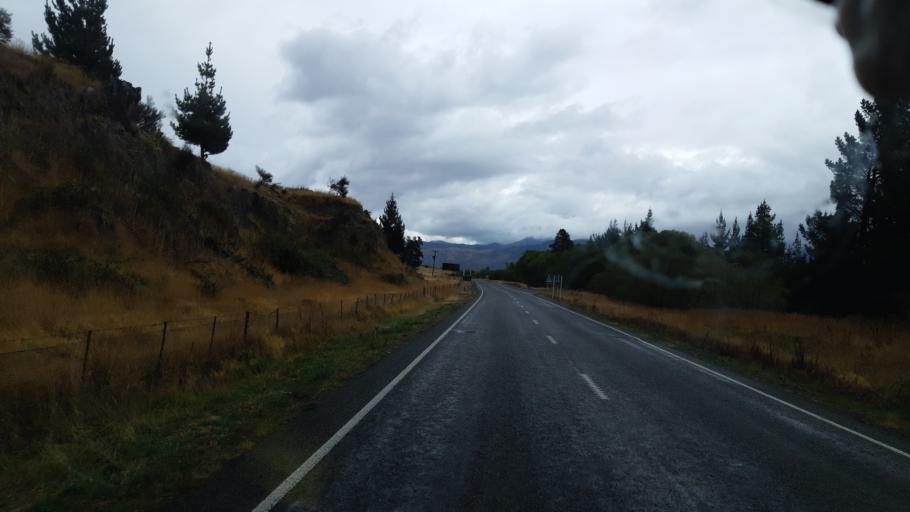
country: NZ
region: Canterbury
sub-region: Hurunui District
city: Amberley
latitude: -42.5801
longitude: 172.7698
